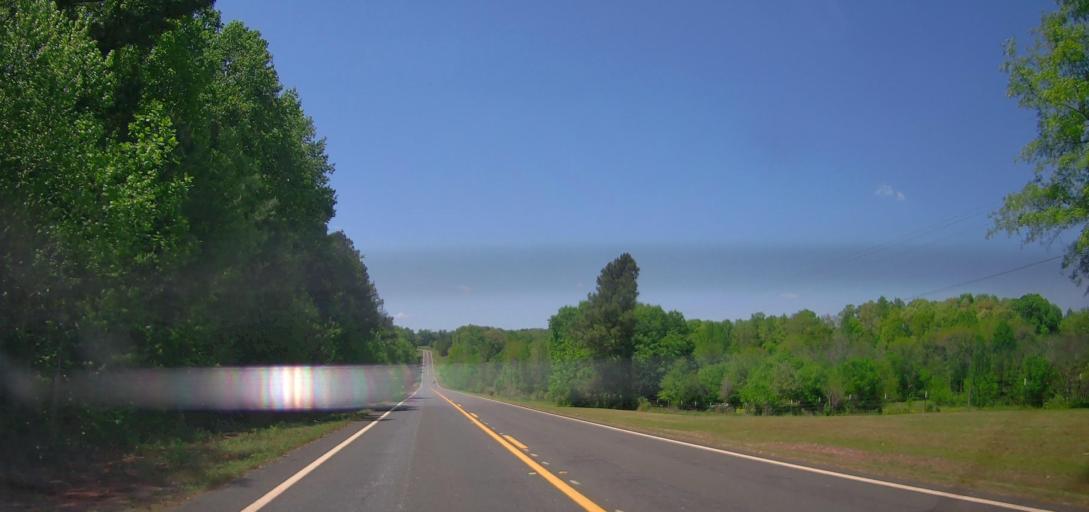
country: US
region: Georgia
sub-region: Jasper County
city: Monticello
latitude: 33.2677
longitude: -83.5850
